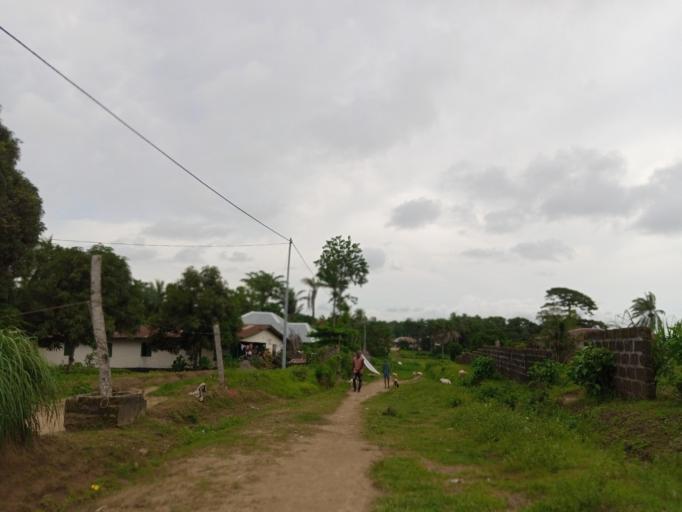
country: SL
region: Northern Province
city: Masoyila
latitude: 8.5984
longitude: -13.2018
